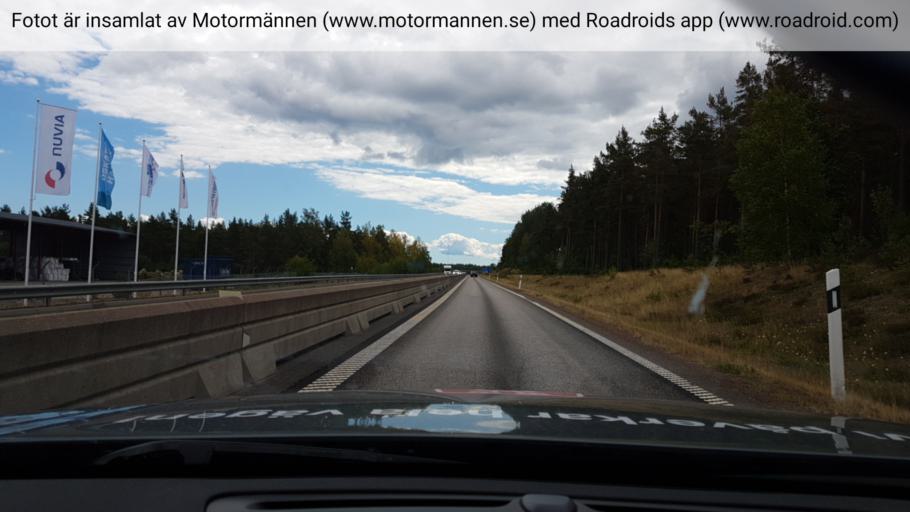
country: SE
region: Kalmar
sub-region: Oskarshamns Kommun
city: Oskarshamn
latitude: 57.3794
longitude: 16.4834
